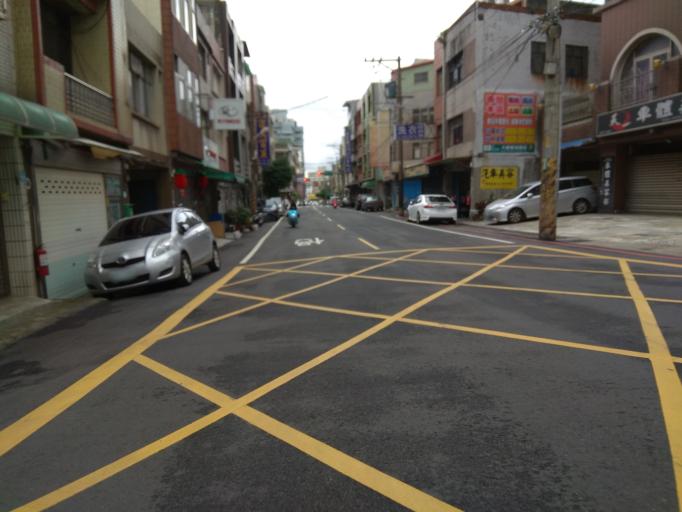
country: TW
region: Taiwan
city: Taoyuan City
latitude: 24.9535
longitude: 121.2125
